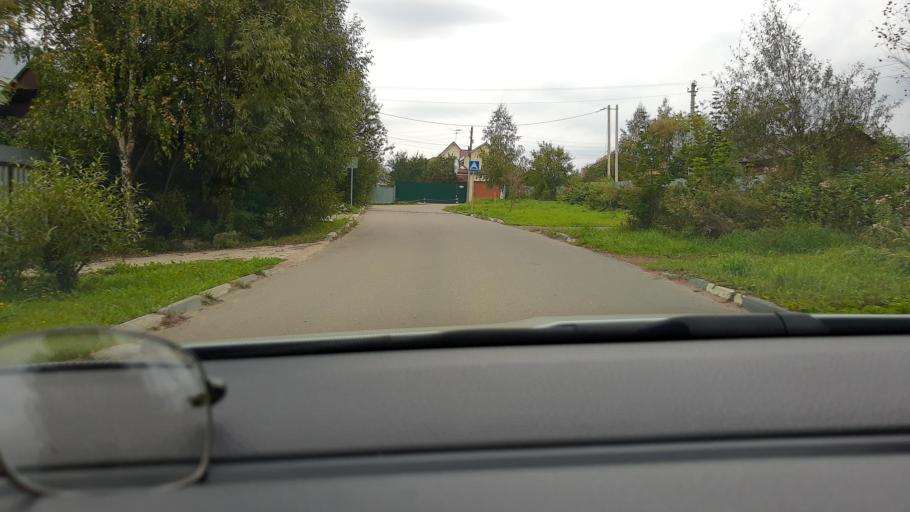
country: RU
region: Moscow
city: Vnukovo
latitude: 55.5940
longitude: 37.1987
